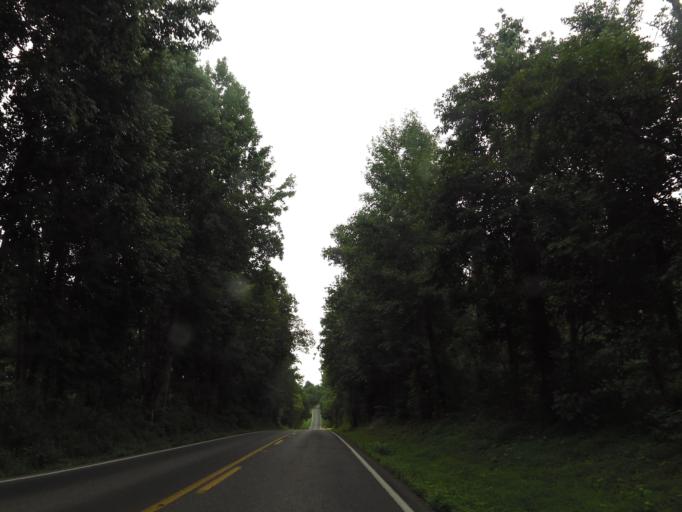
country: US
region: Kentucky
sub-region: Ballard County
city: Wickliffe
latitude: 36.9747
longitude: -89.0481
